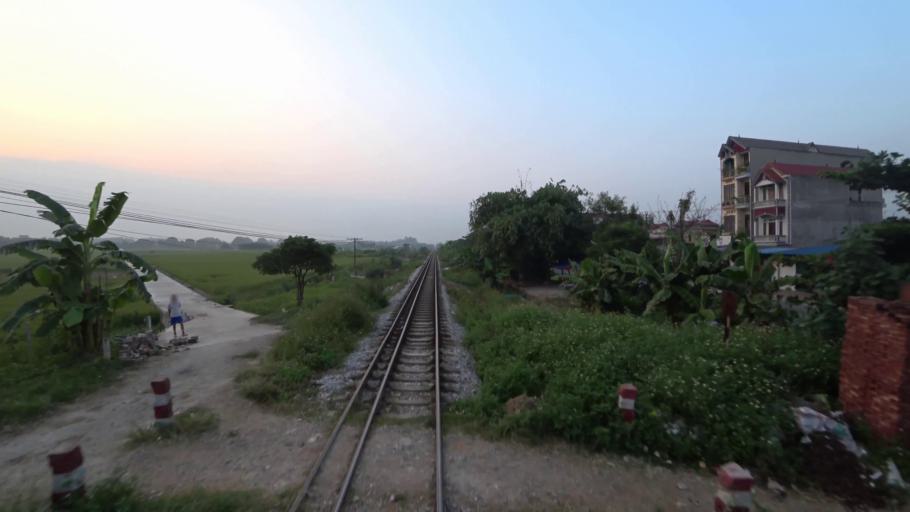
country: VN
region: Ha Noi
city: Dong Anh
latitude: 21.1286
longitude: 105.8779
